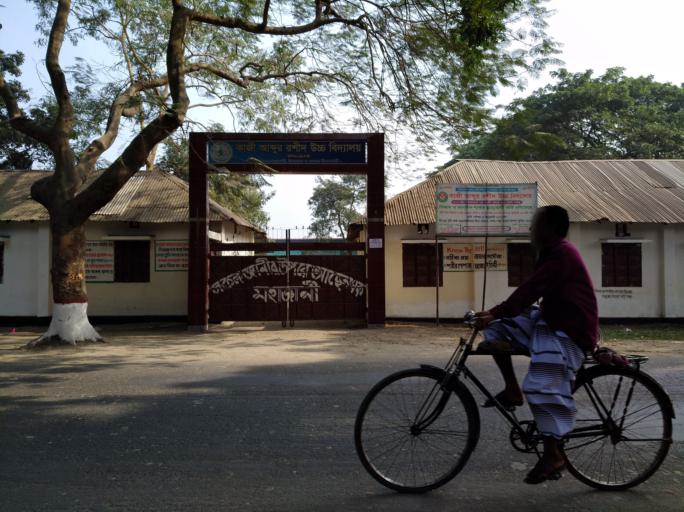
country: BD
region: Rajshahi
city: Saidpur
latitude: 25.8494
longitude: 88.8730
